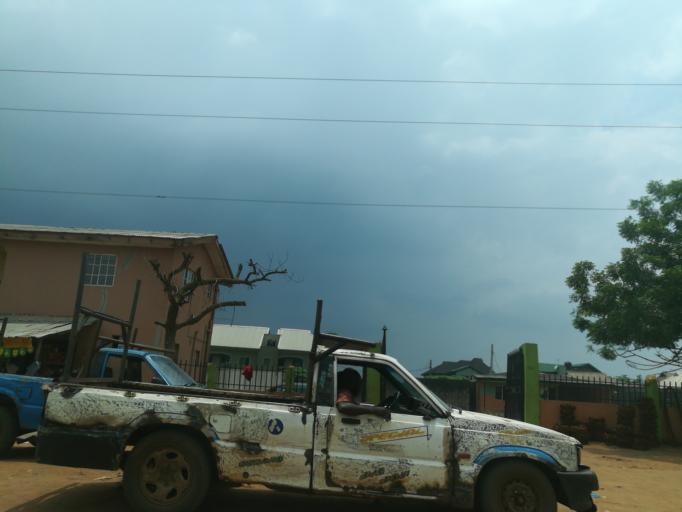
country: NG
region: Lagos
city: Ikorodu
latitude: 6.6132
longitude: 3.5772
